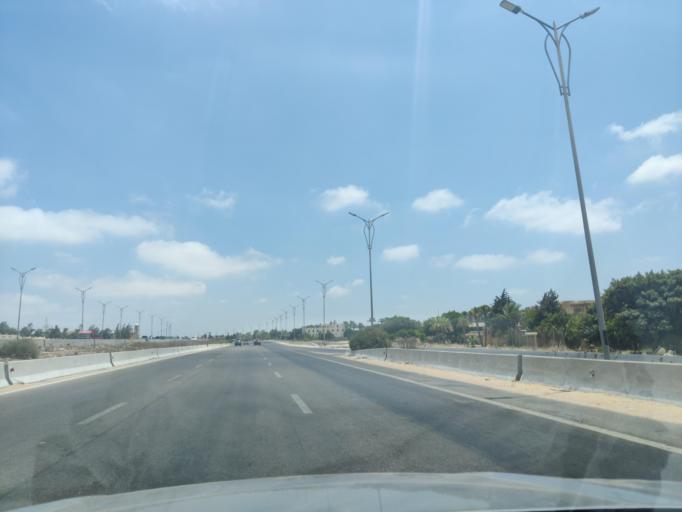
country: EG
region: Alexandria
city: Alexandria
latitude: 31.0116
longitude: 29.7488
